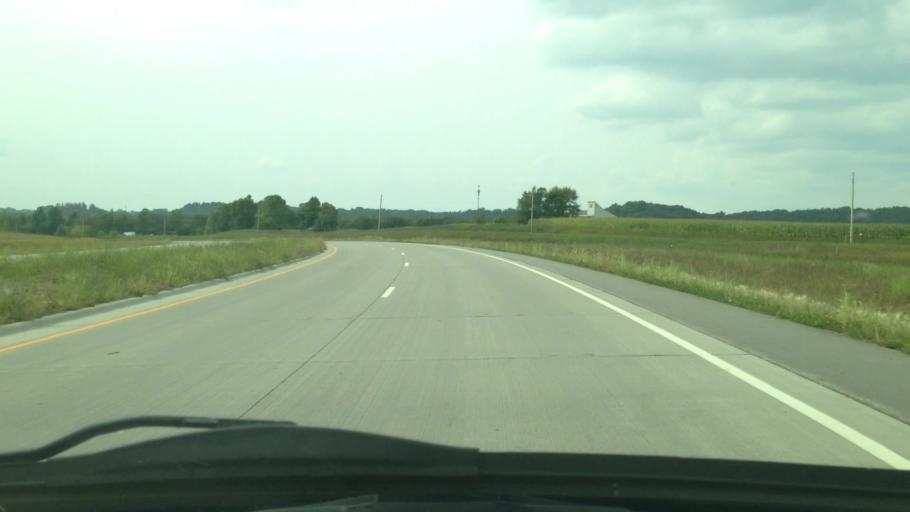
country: US
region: Minnesota
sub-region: Olmsted County
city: Rochester
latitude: 44.0797
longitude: -92.4605
